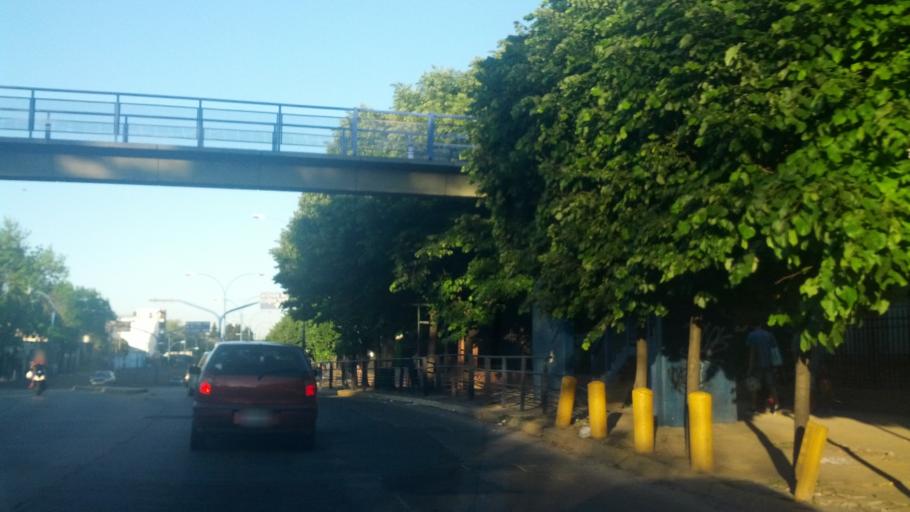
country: AR
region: Buenos Aires
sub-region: Partido de Lomas de Zamora
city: Lomas de Zamora
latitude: -34.7813
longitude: -58.3992
